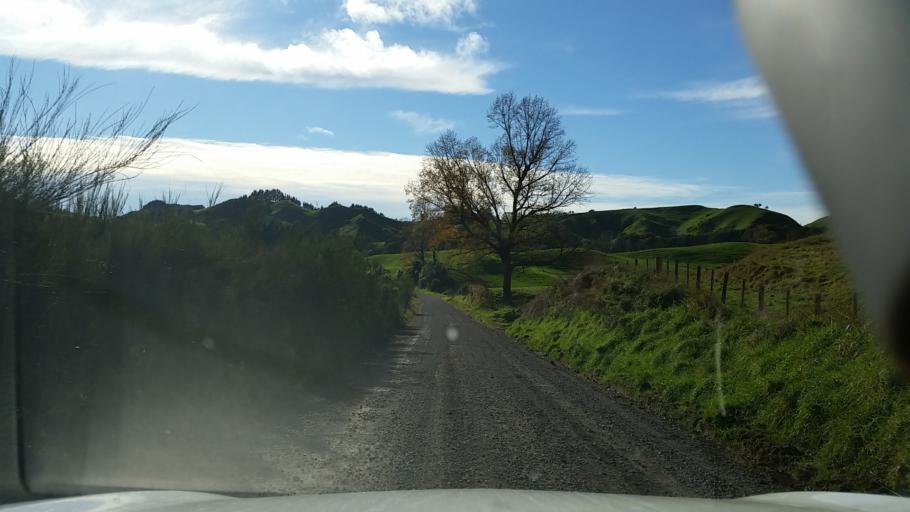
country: NZ
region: Bay of Plenty
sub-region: Rotorua District
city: Rotorua
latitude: -38.3623
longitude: 176.2089
